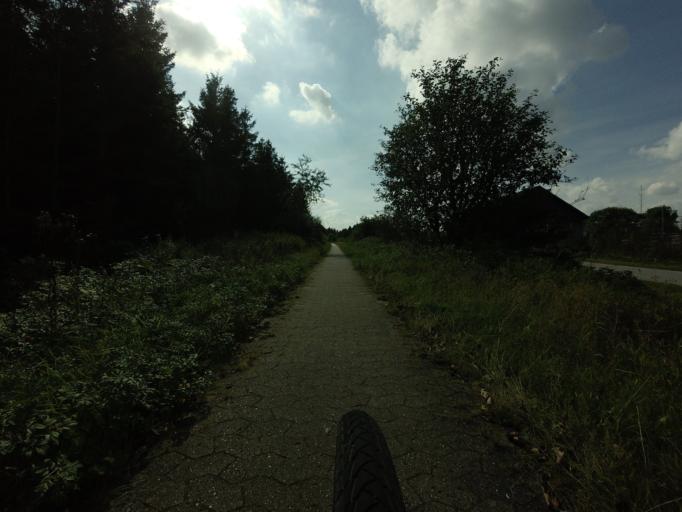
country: DK
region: Central Jutland
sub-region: Viborg Kommune
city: Karup
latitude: 56.2789
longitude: 9.1229
